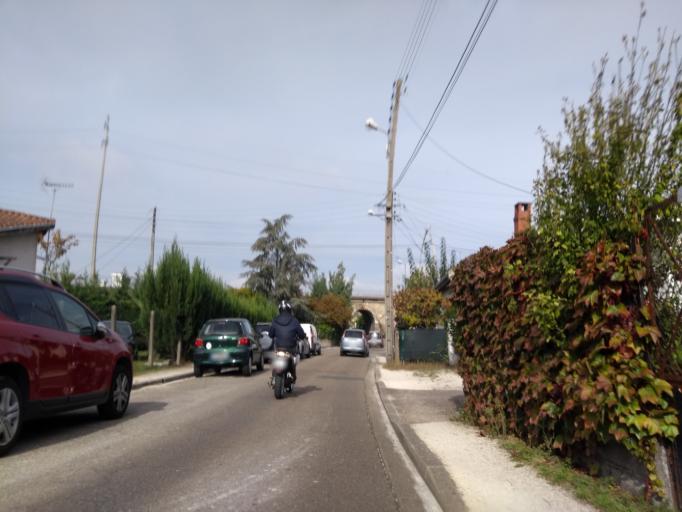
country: FR
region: Aquitaine
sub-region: Departement de la Gironde
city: Talence
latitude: 44.8089
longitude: -0.6176
